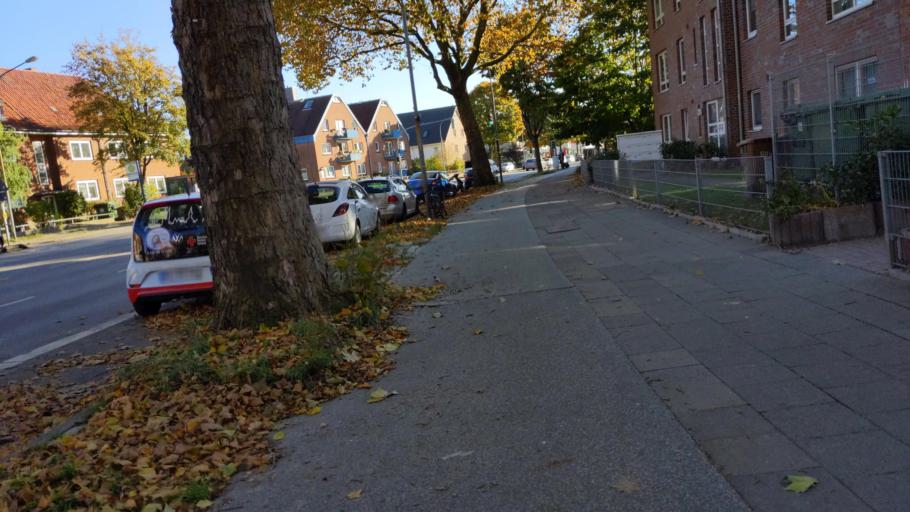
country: DE
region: Schleswig-Holstein
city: Luebeck
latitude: 53.8467
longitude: 10.7077
